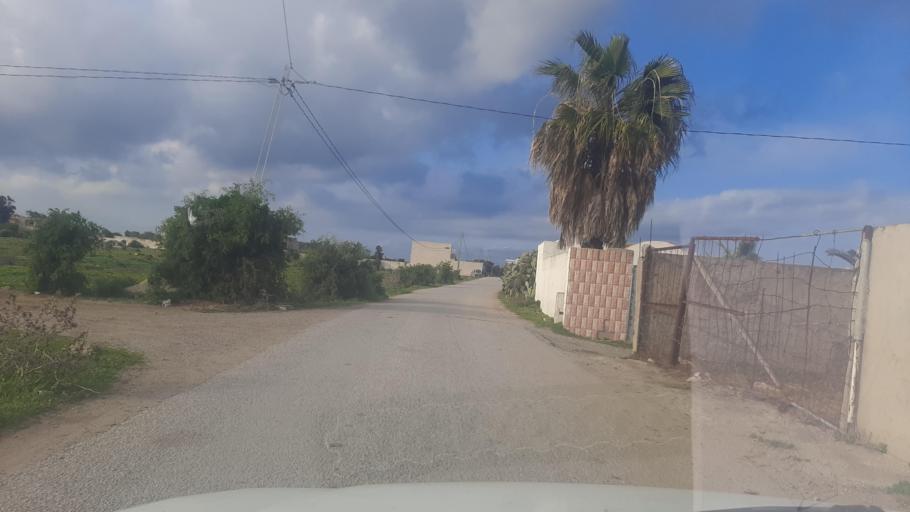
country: TN
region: Nabul
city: Manzil Bu Zalafah
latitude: 36.7145
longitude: 10.4977
